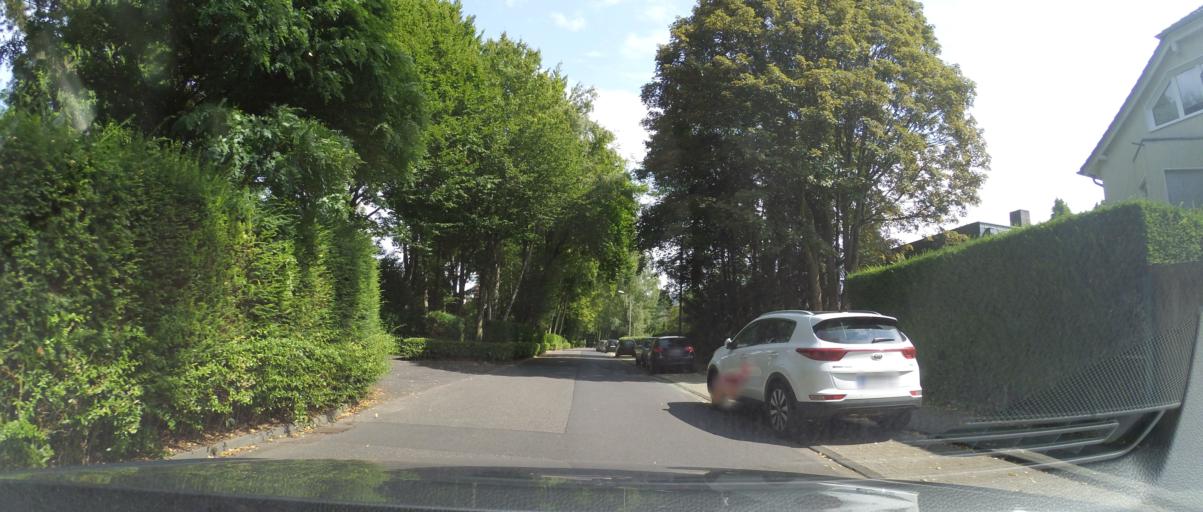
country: DE
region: North Rhine-Westphalia
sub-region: Regierungsbezirk Koln
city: Mengenich
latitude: 50.9361
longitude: 6.8624
